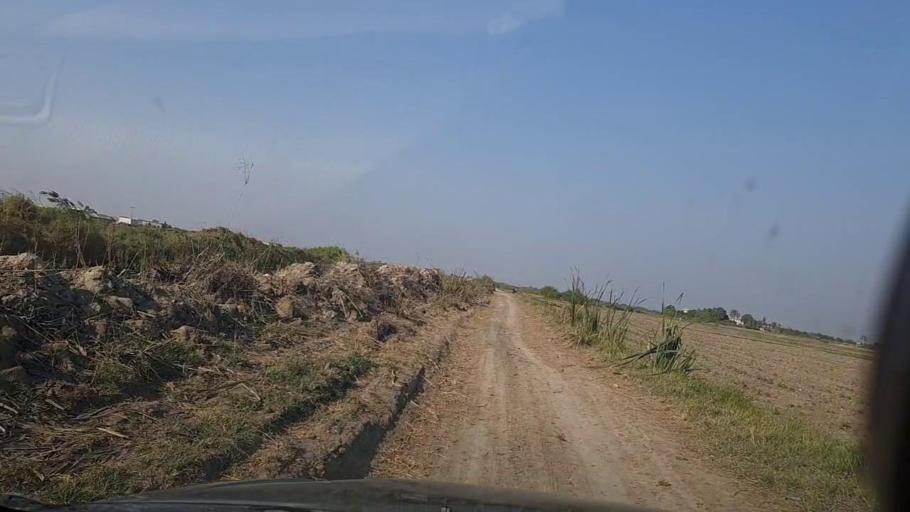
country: PK
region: Sindh
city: Thatta
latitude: 24.5871
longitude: 67.8822
